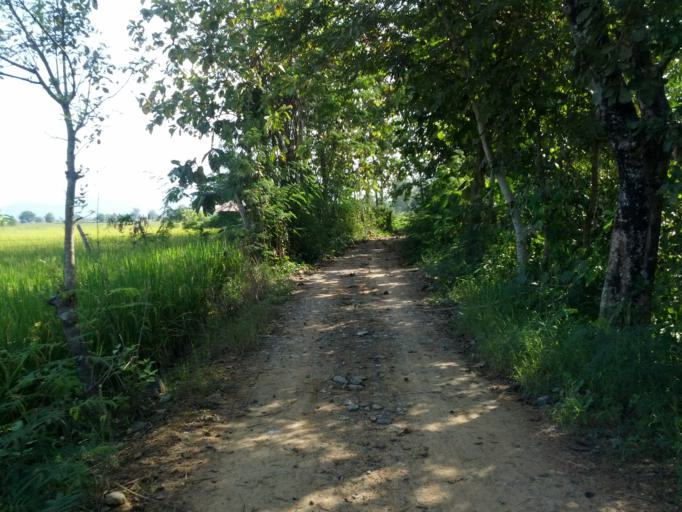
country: TH
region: Chiang Mai
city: San Kamphaeng
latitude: 18.7689
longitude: 99.1285
